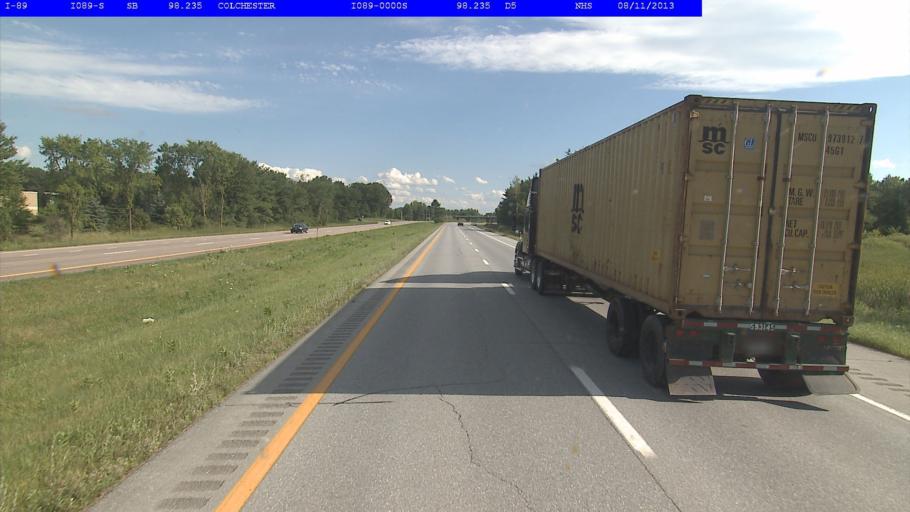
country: US
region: Vermont
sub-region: Chittenden County
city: Colchester
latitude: 44.5950
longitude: -73.1719
